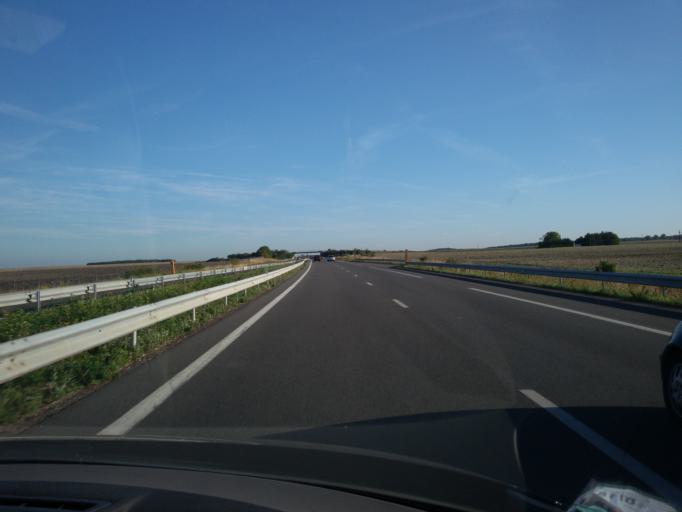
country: FR
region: Centre
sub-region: Departement du Cher
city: Chateauneuf-sur-Cher
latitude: 46.8199
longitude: 2.4130
